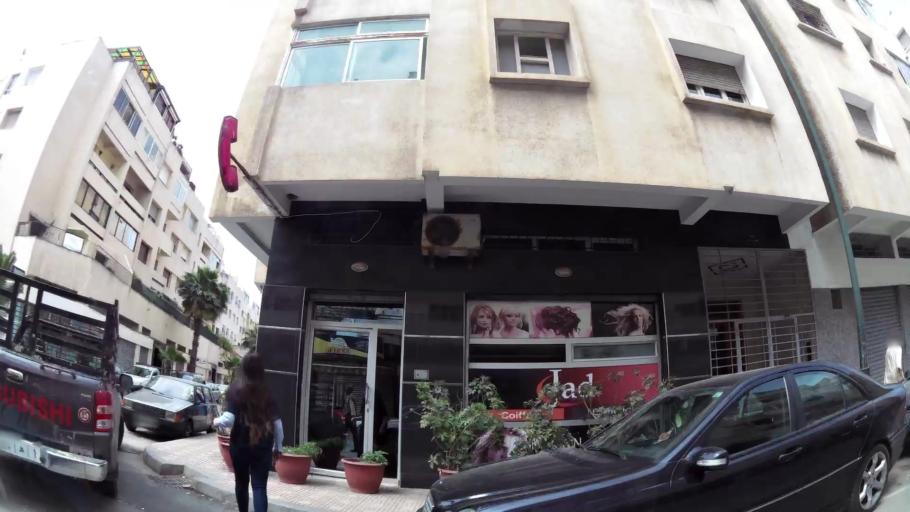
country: MA
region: Rabat-Sale-Zemmour-Zaer
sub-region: Rabat
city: Rabat
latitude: 34.0176
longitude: -6.8510
